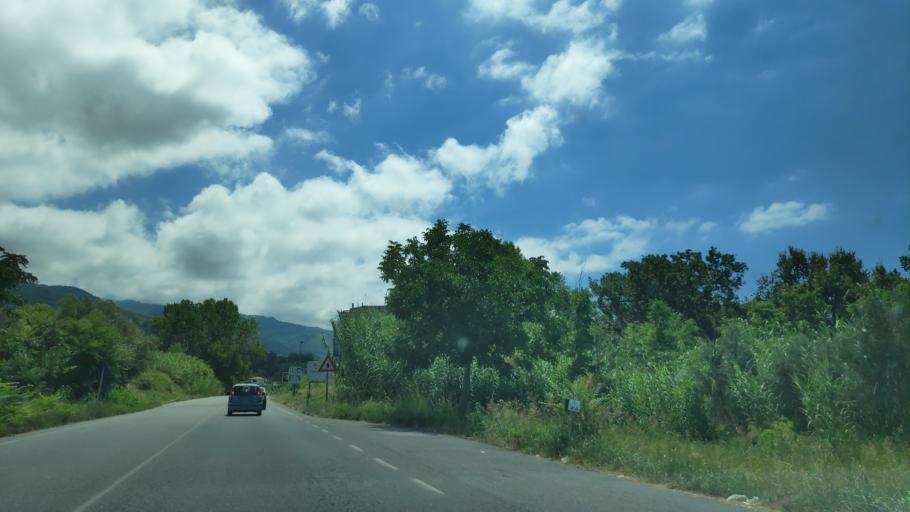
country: IT
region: Calabria
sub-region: Provincia di Cosenza
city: Scarcelli
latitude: 39.3849
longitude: 16.0246
